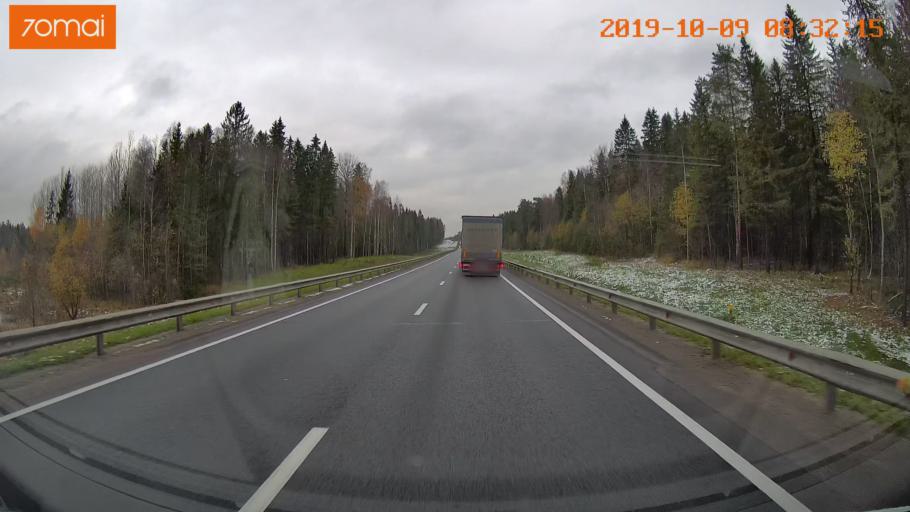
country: RU
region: Vologda
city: Gryazovets
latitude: 58.8641
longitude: 40.1982
